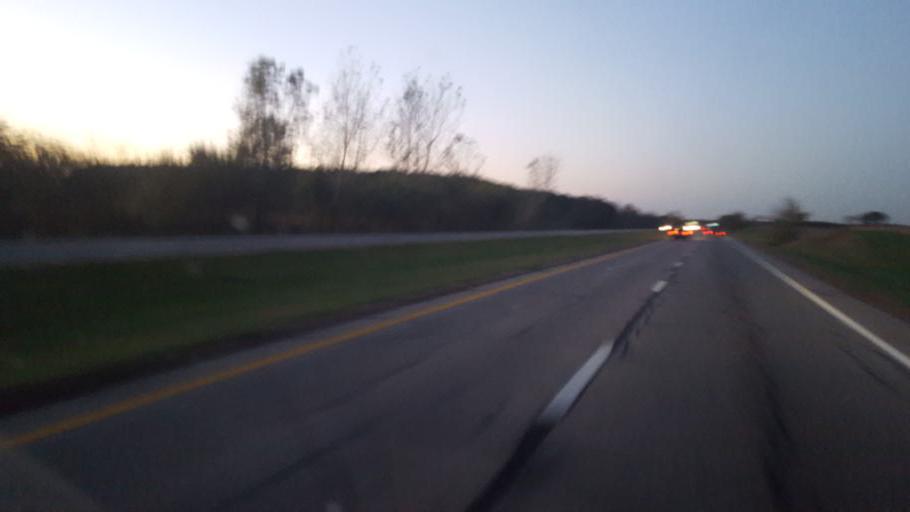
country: US
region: Ohio
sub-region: Ross County
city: Kingston
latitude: 39.4808
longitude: -82.9711
